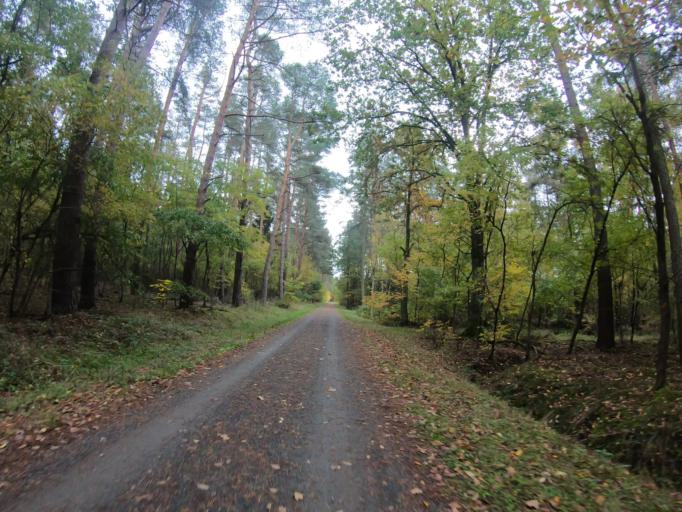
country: DE
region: Lower Saxony
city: Isenbuttel
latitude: 52.4527
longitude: 10.5661
